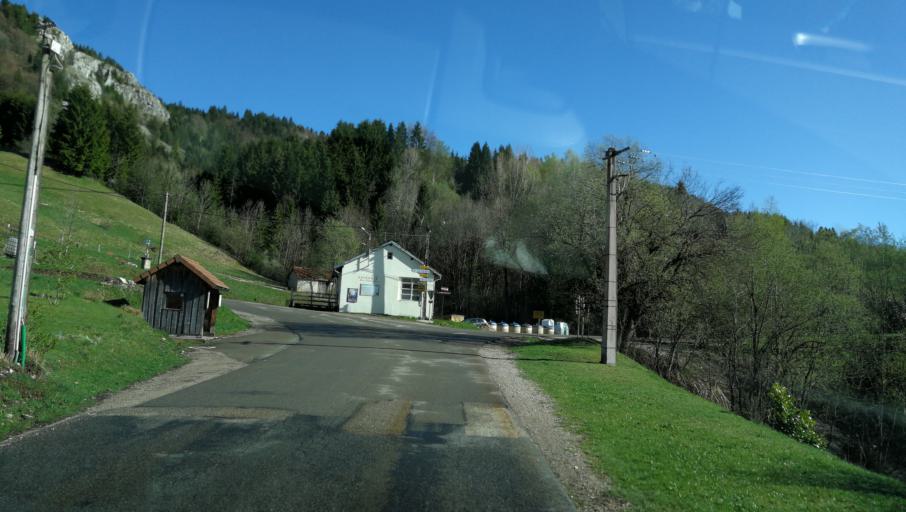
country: FR
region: Franche-Comte
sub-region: Departement du Jura
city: Lavans-les-Saint-Claude
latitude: 46.2958
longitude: 5.8189
